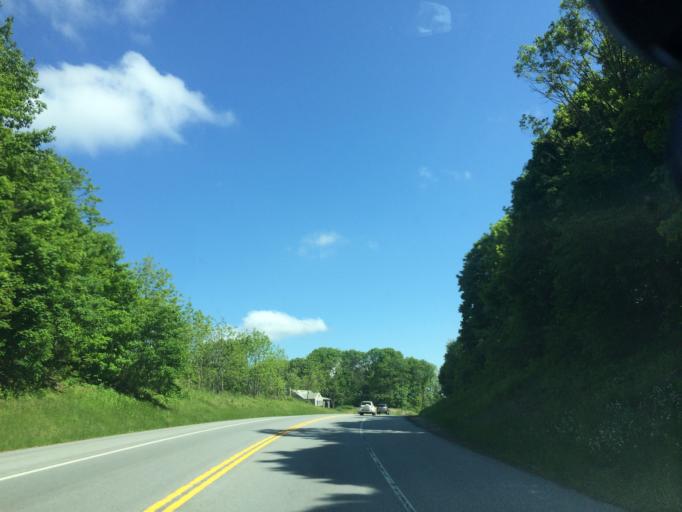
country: US
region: Maryland
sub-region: Carroll County
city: Manchester
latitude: 39.7108
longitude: -76.9175
